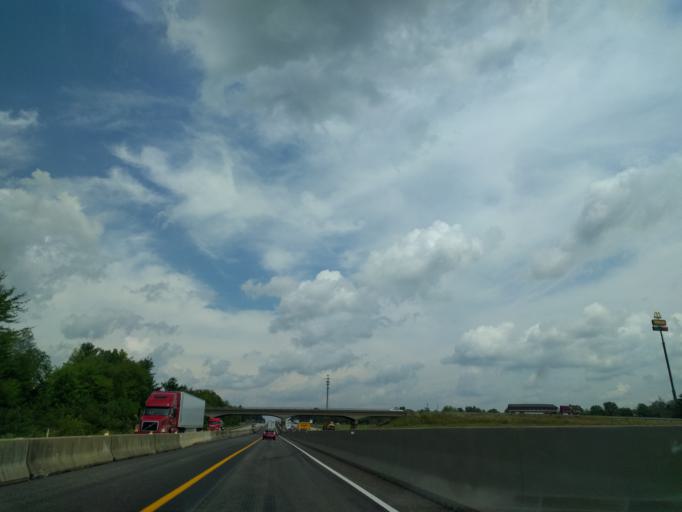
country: US
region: Kentucky
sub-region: Hardin County
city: Elizabethtown
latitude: 37.5946
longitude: -85.8691
